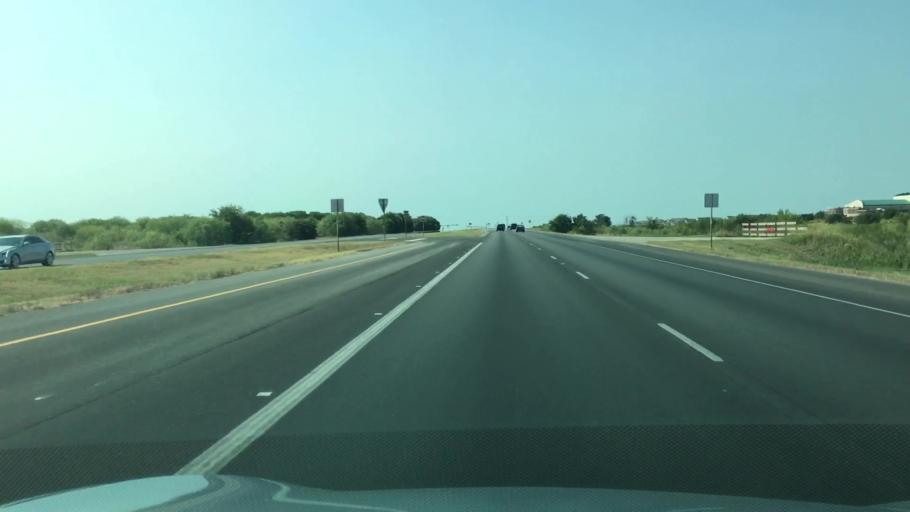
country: US
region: Texas
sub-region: Hays County
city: Kyle
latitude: 30.0355
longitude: -97.8725
